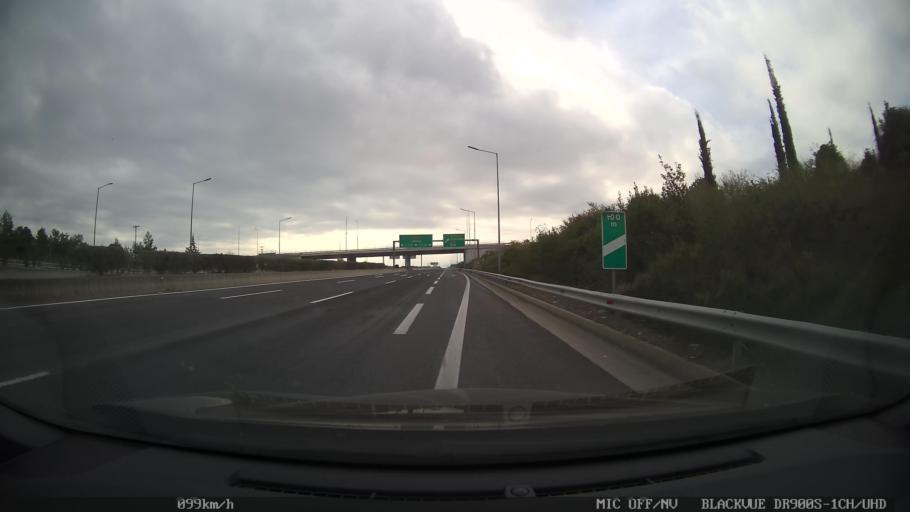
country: GR
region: Central Macedonia
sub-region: Nomos Pierias
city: Litochoro
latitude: 40.1339
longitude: 22.5455
